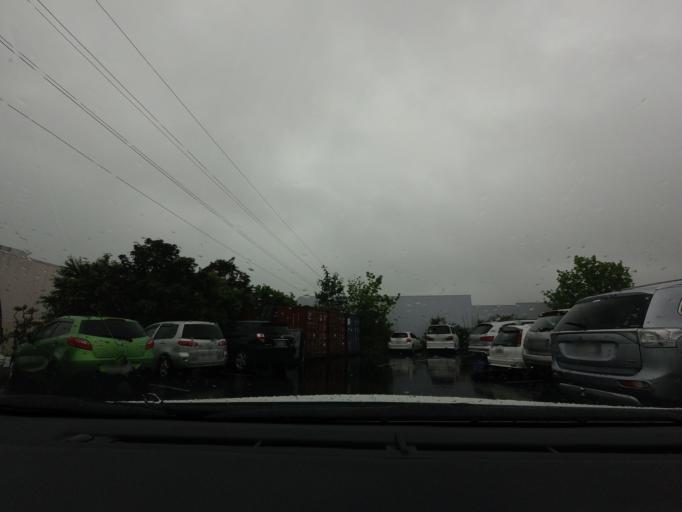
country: NZ
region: Auckland
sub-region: Auckland
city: North Shore
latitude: -36.7658
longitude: 174.7367
